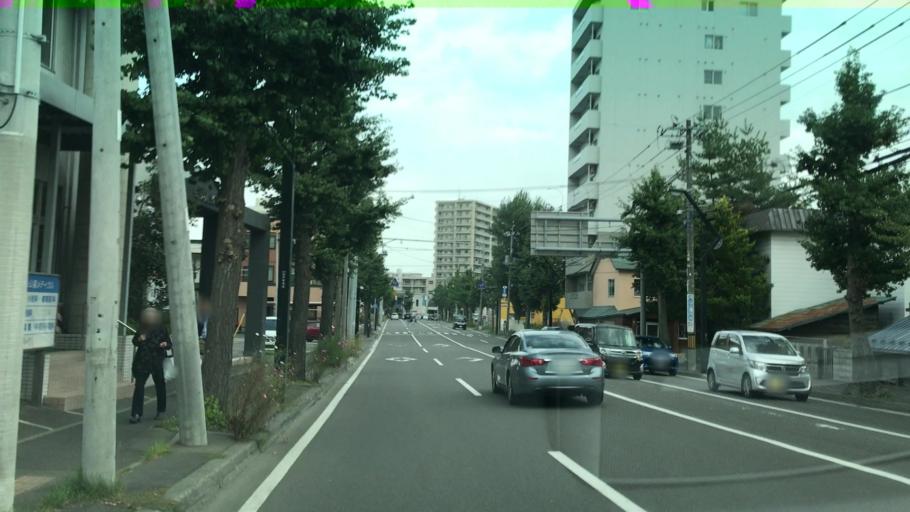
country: JP
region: Hokkaido
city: Sapporo
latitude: 43.0462
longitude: 141.3235
